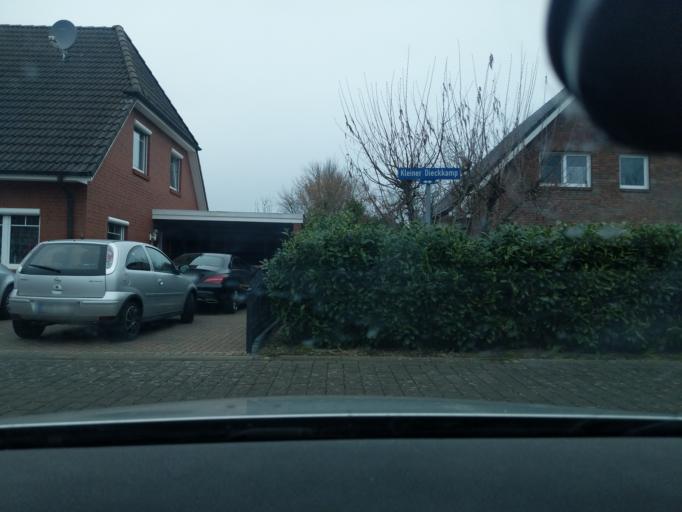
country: DE
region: Lower Saxony
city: Bremervorde
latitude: 53.4787
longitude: 9.1728
